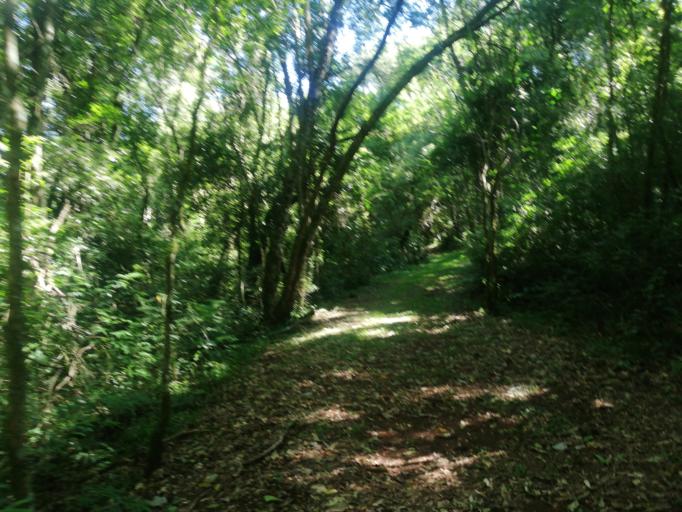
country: AR
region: Misiones
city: Cerro Azul
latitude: -27.7510
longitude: -55.5612
